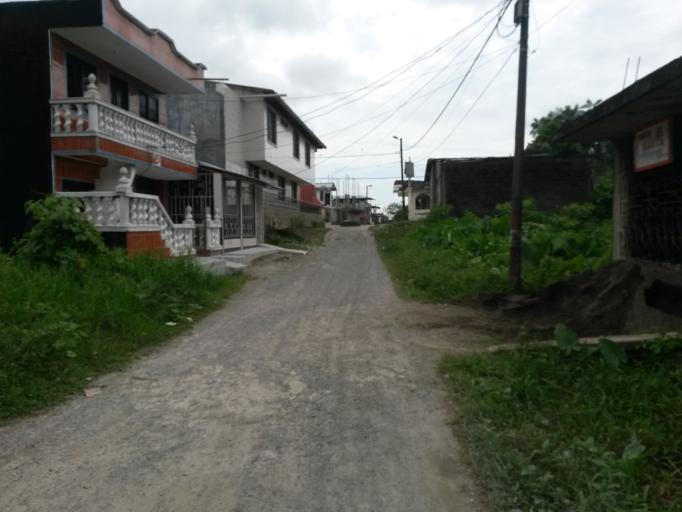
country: CO
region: Cauca
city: Guapi
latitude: 2.5712
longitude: -77.8883
